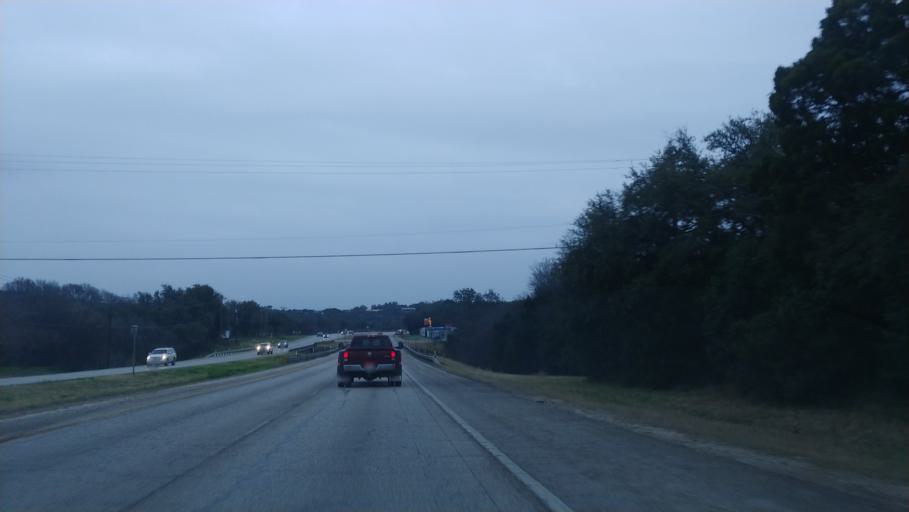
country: US
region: Texas
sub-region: Bexar County
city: Helotes
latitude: 29.5806
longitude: -98.6917
